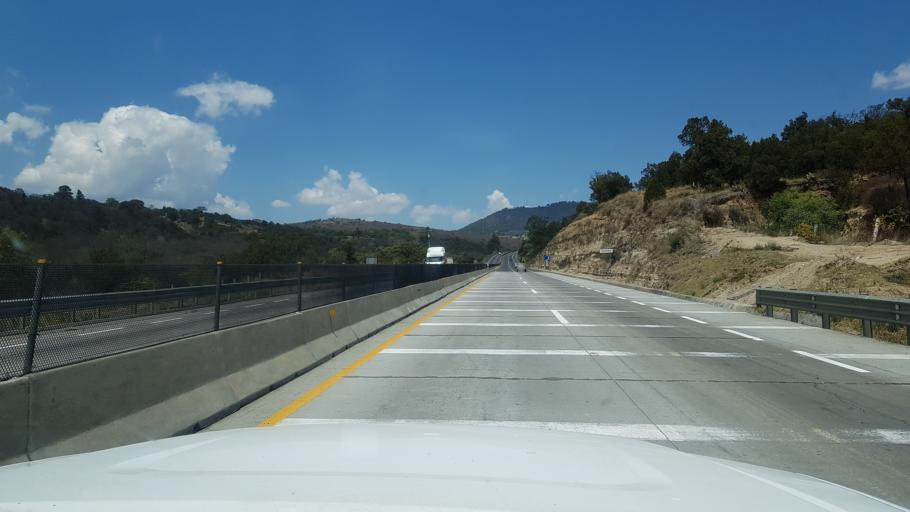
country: MX
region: Tlaxcala
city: Espanita
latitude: 19.4464
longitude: -98.4385
